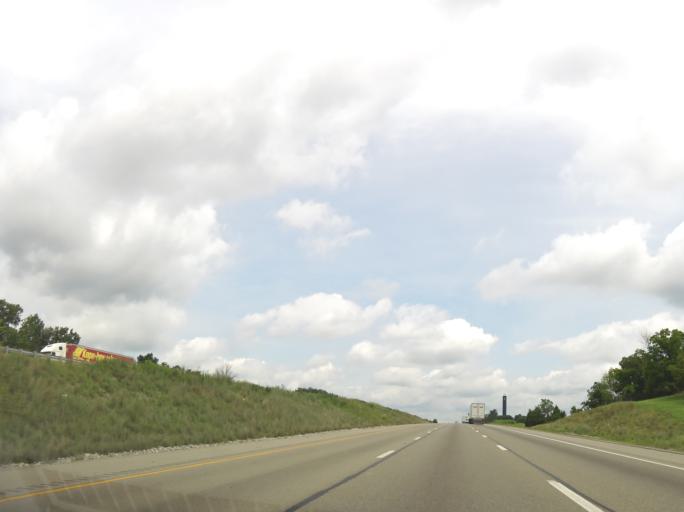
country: US
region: Kentucky
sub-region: Grant County
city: Williamstown
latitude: 38.5186
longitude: -84.5875
